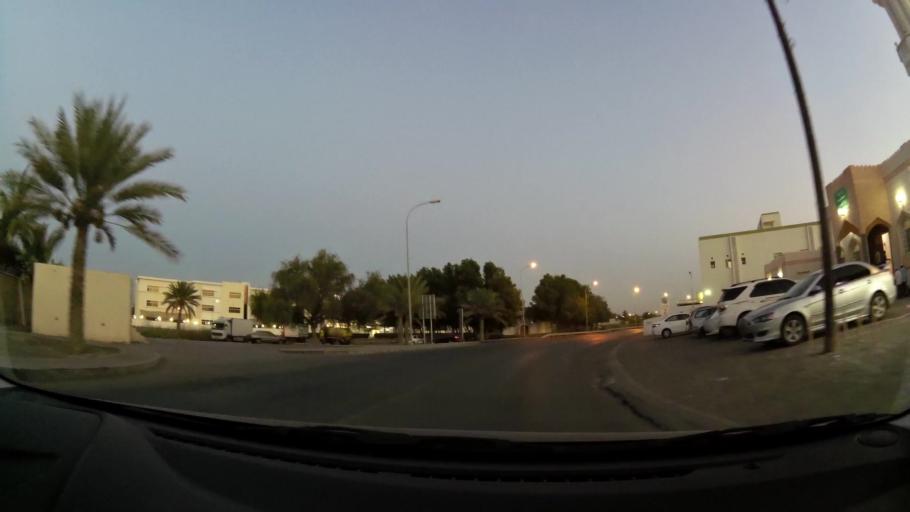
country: OM
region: Muhafazat Masqat
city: As Sib al Jadidah
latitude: 23.6750
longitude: 58.1917
